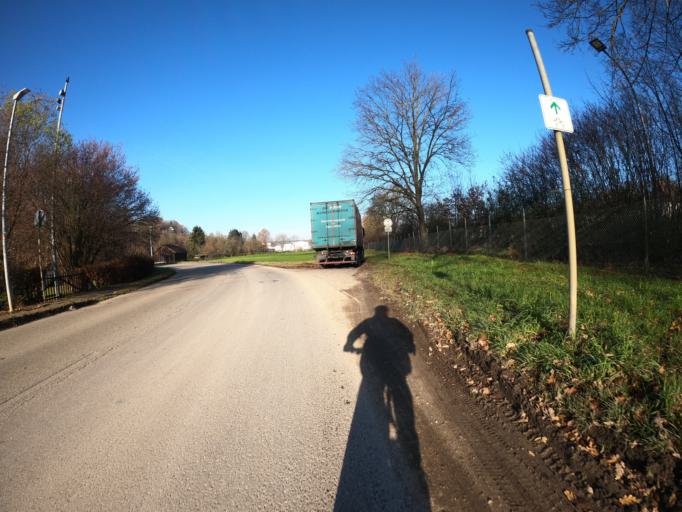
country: DE
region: Baden-Wuerttemberg
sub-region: Regierungsbezirk Stuttgart
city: Goeppingen
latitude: 48.6854
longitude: 9.6710
